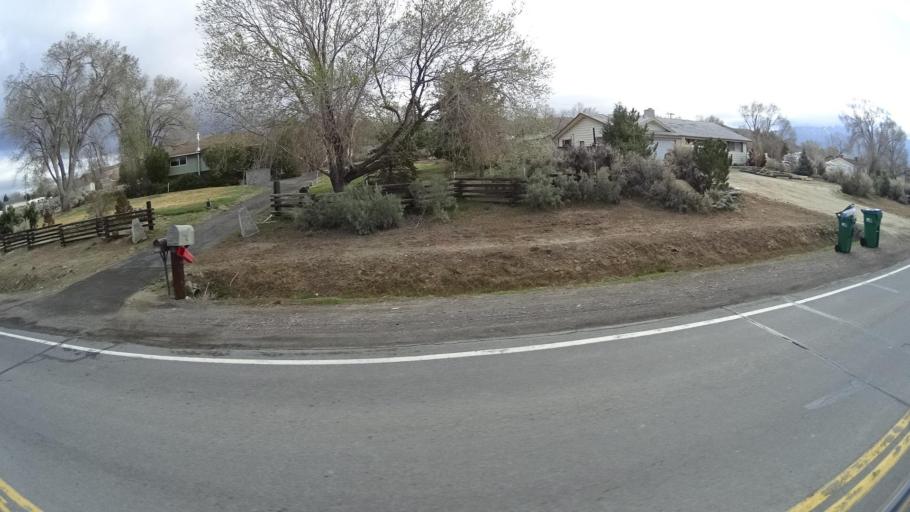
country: US
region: Nevada
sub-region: Storey County
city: Virginia City
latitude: 39.3087
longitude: -119.7883
